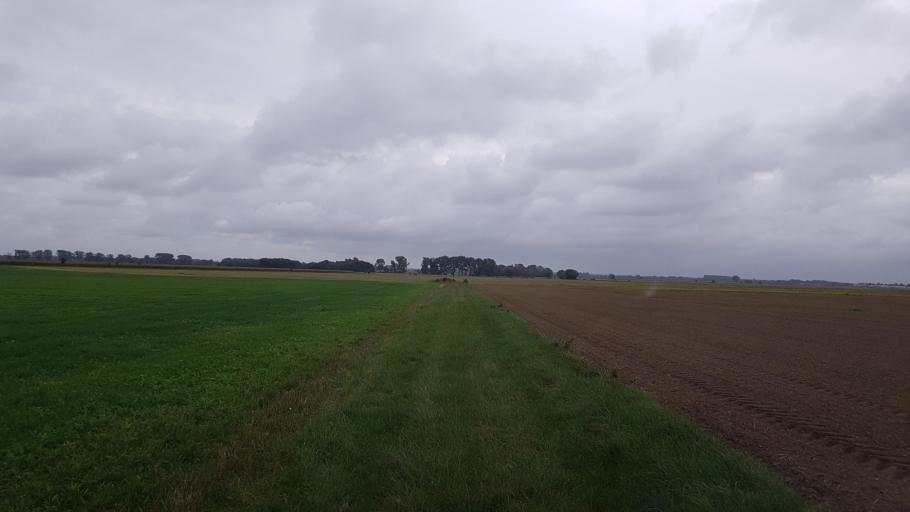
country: DE
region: Brandenburg
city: Doberlug-Kirchhain
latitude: 51.6825
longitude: 13.5258
